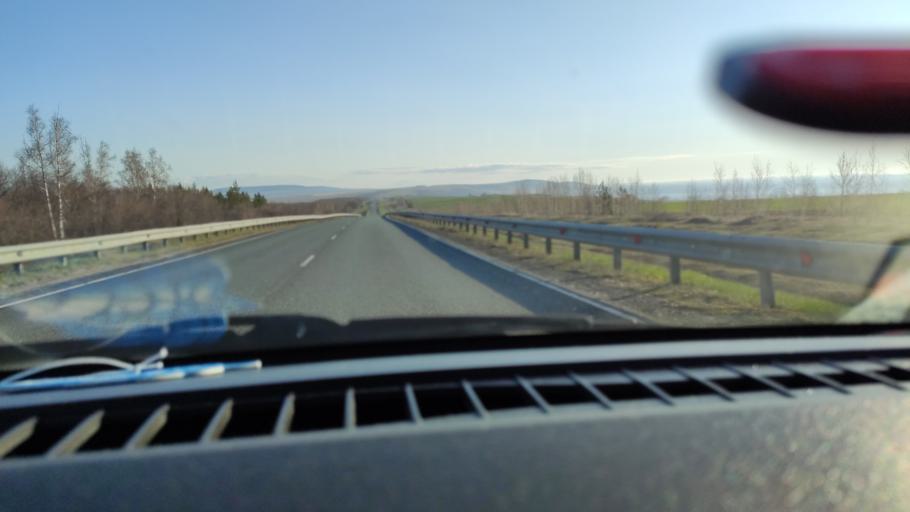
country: RU
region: Saratov
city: Balakovo
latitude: 52.1705
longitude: 47.8299
